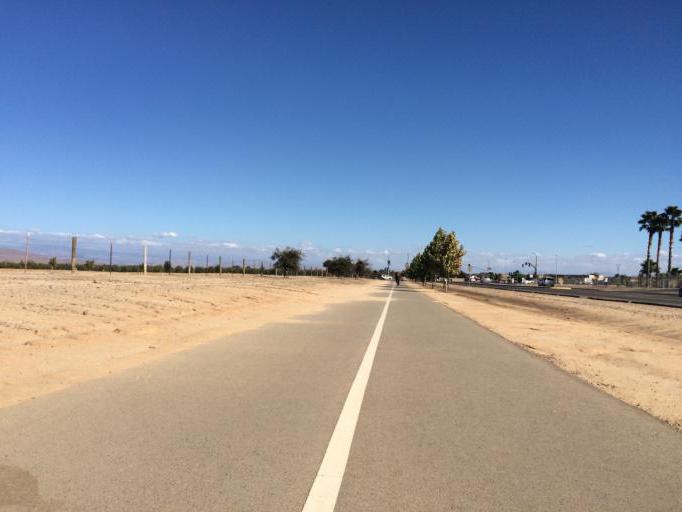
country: US
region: California
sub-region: Fresno County
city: Clovis
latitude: 36.8670
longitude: -119.7323
